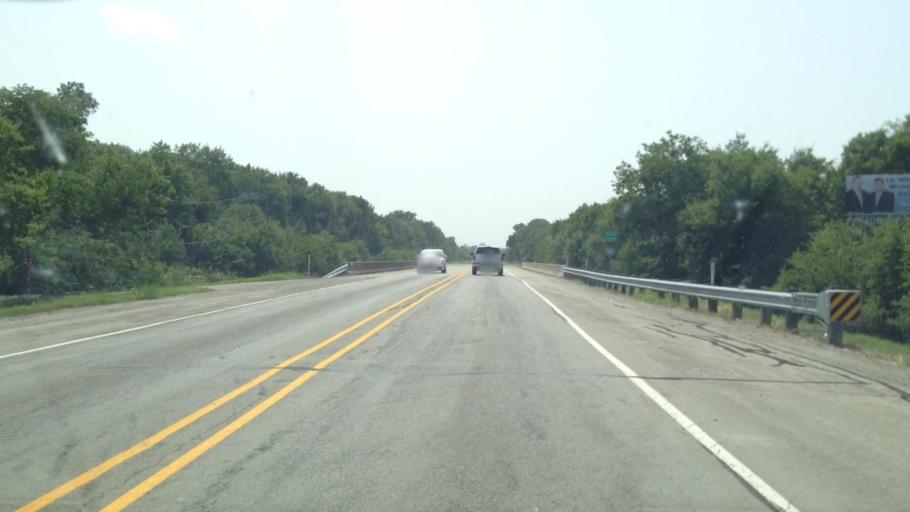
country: US
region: Texas
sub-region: Hunt County
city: Greenville
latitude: 33.1395
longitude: -96.0814
